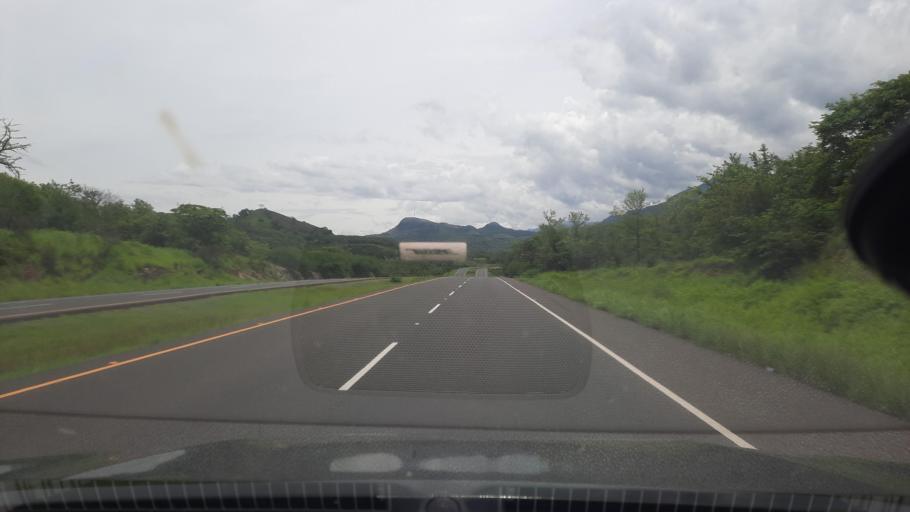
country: HN
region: Valle
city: Aramecina
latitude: 13.7605
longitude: -87.7091
